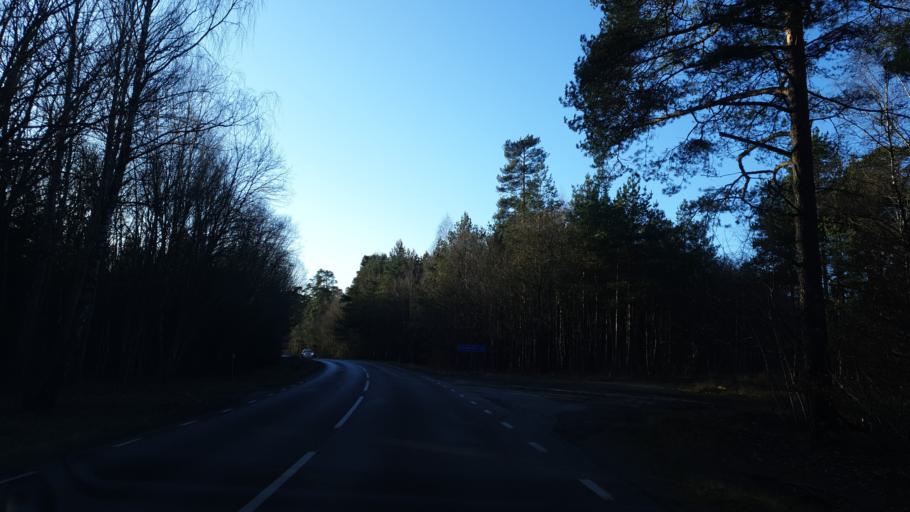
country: SE
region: Blekinge
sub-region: Ronneby Kommun
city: Kallinge
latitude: 56.2159
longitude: 15.3945
